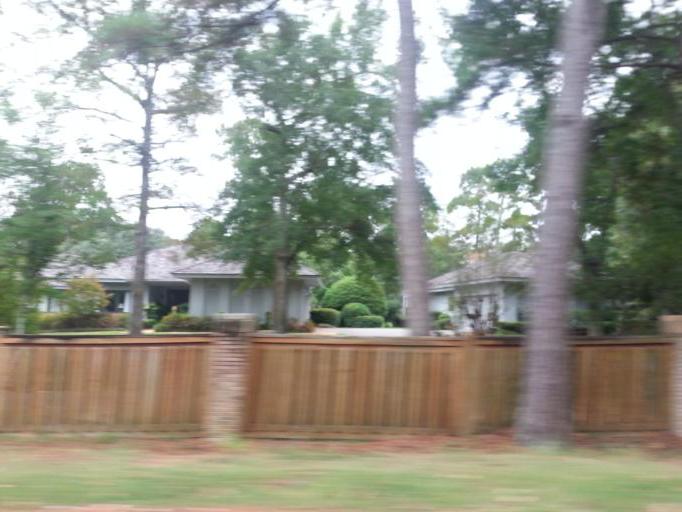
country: US
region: Alabama
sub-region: Baldwin County
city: Point Clear
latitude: 30.4899
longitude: -87.9280
